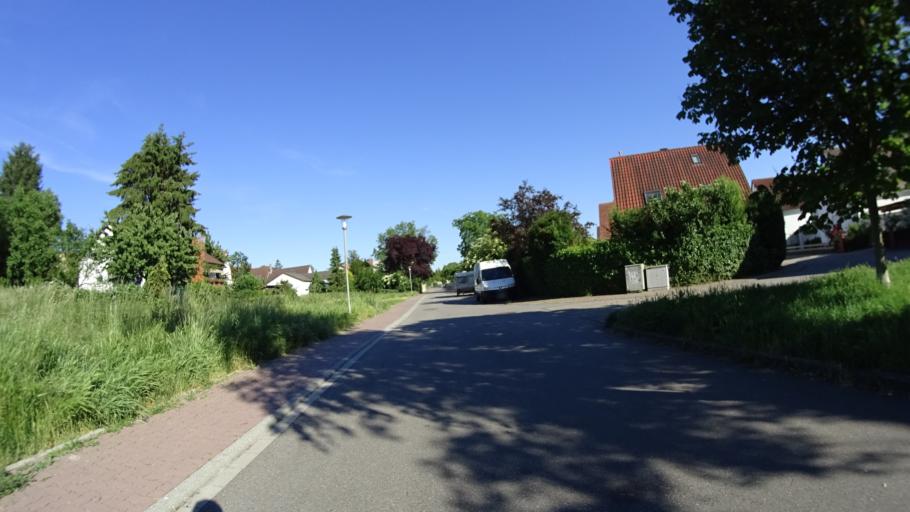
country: DE
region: Baden-Wuerttemberg
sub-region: Karlsruhe Region
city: Eggenstein-Leopoldshafen
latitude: 49.0999
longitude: 8.3880
